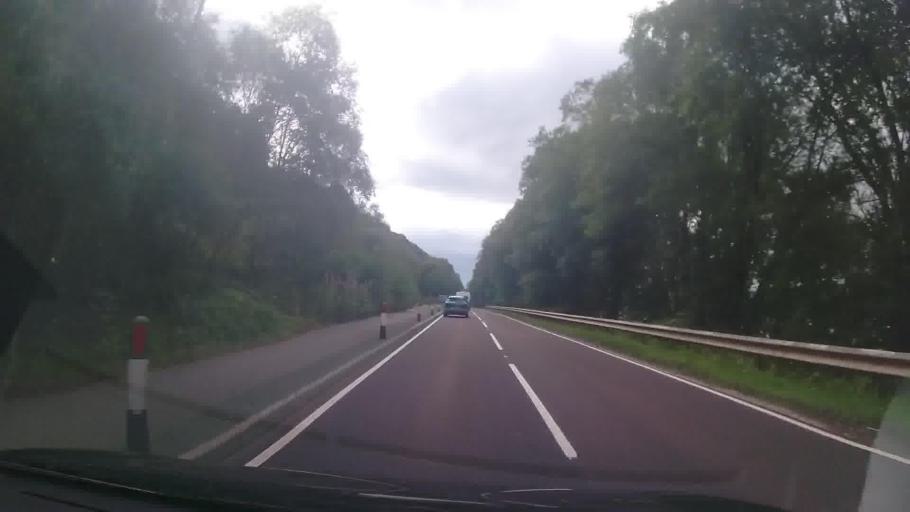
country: GB
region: Scotland
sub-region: Argyll and Bute
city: Oban
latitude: 56.6208
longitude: -5.3230
